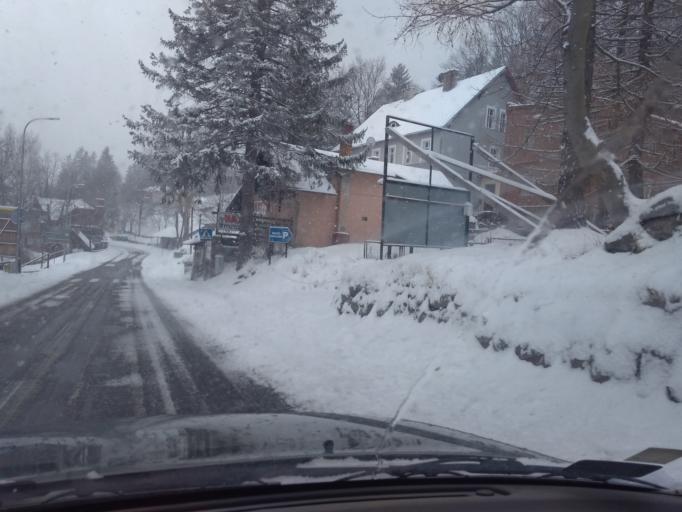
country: PL
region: Lower Silesian Voivodeship
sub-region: Powiat jeleniogorski
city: Karpacz
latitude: 50.7801
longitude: 15.7247
